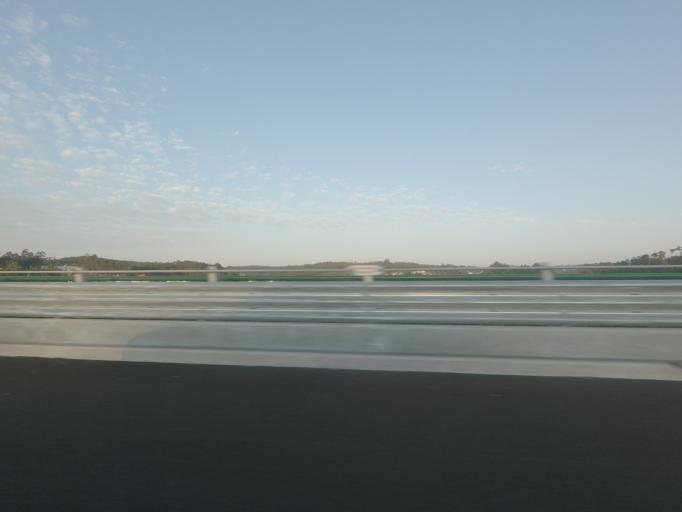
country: PT
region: Leiria
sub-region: Leiria
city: Caranguejeira
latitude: 39.8059
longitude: -8.7225
